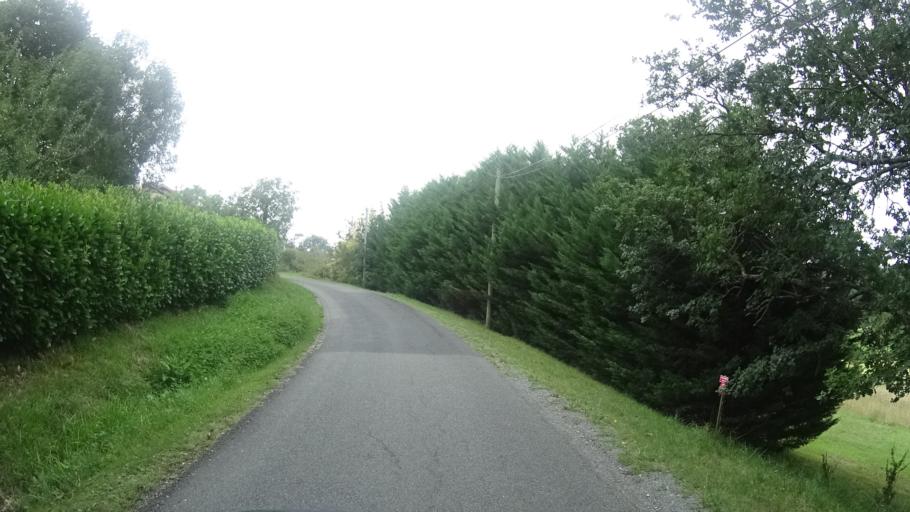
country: FR
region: Aquitaine
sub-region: Departement de la Dordogne
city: Neuvic
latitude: 45.0412
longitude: 0.5297
